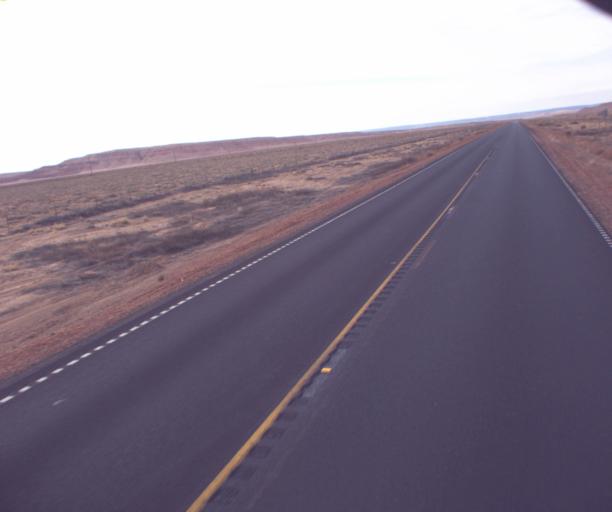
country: US
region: Arizona
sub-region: Apache County
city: Chinle
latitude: 36.1360
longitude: -109.6110
